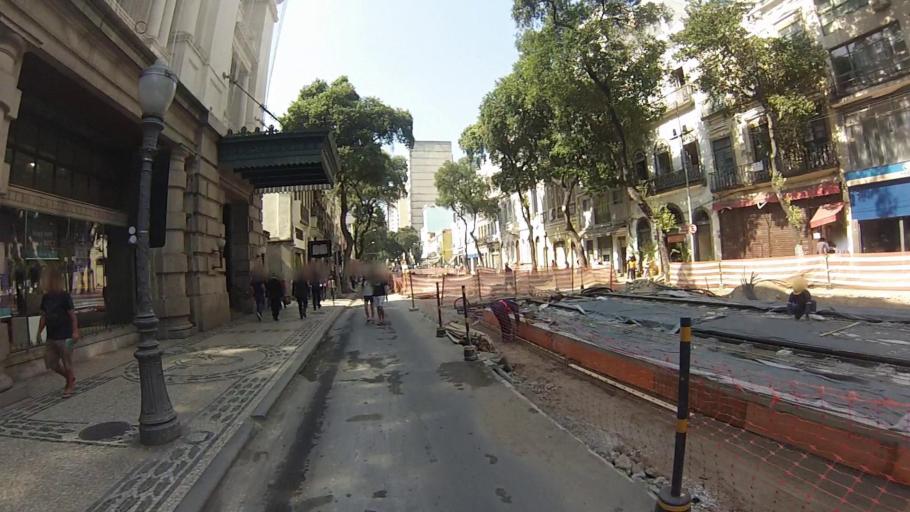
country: BR
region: Rio de Janeiro
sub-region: Rio De Janeiro
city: Rio de Janeiro
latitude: -22.9027
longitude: -43.1869
